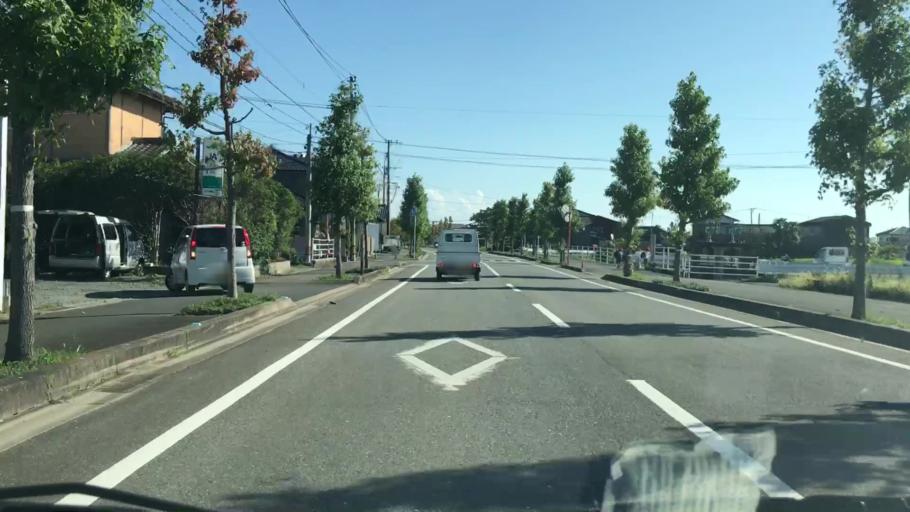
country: JP
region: Saga Prefecture
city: Okawa
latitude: 33.1875
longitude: 130.3141
